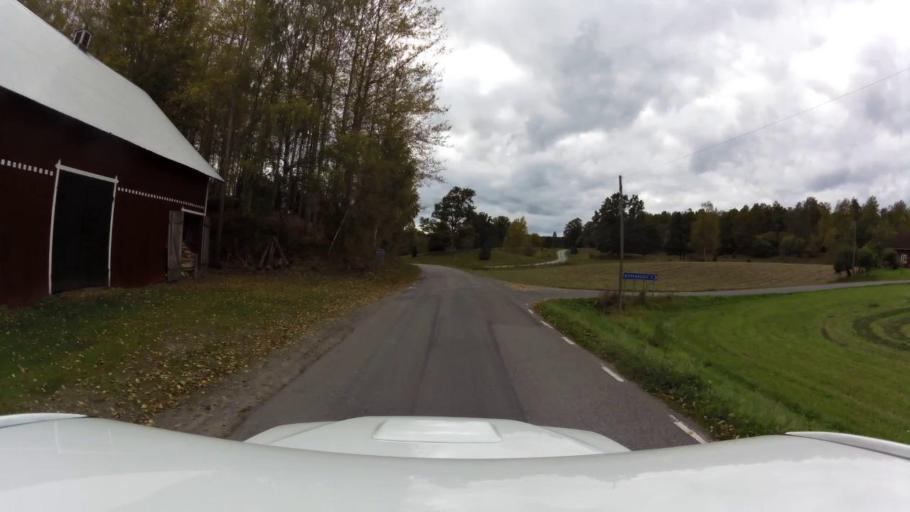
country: SE
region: OEstergoetland
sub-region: Kinda Kommun
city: Rimforsa
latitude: 58.1949
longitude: 15.5681
